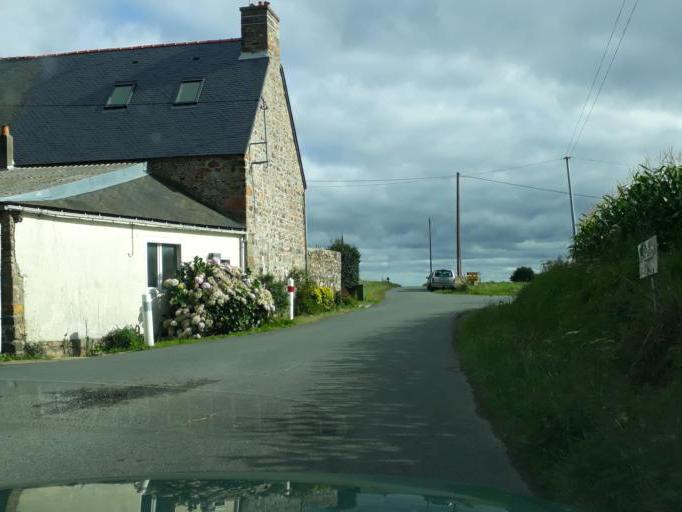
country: FR
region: Brittany
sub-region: Departement des Cotes-d'Armor
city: Ploubazlanec
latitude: 48.8061
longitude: -3.0349
